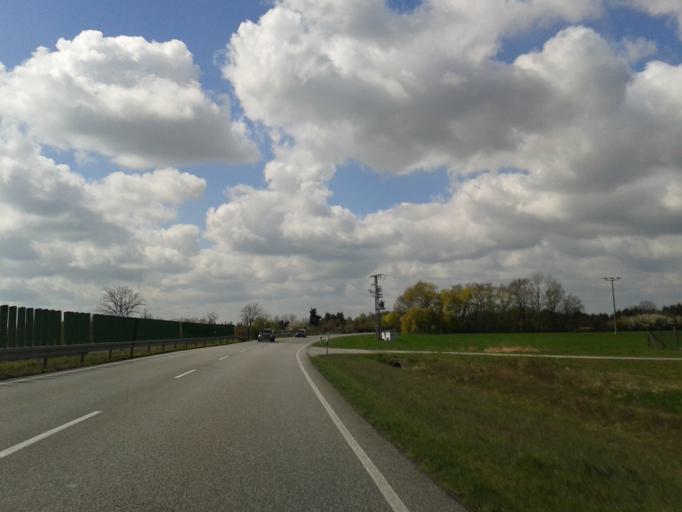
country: DE
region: Saxony-Anhalt
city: Salzwedel
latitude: 52.8589
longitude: 11.1276
